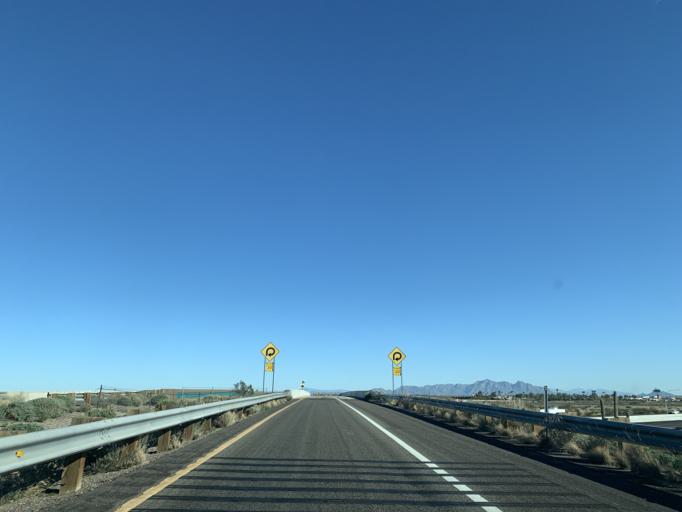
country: US
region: Arizona
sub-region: Pinal County
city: Arizona City
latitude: 32.8193
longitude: -111.6846
